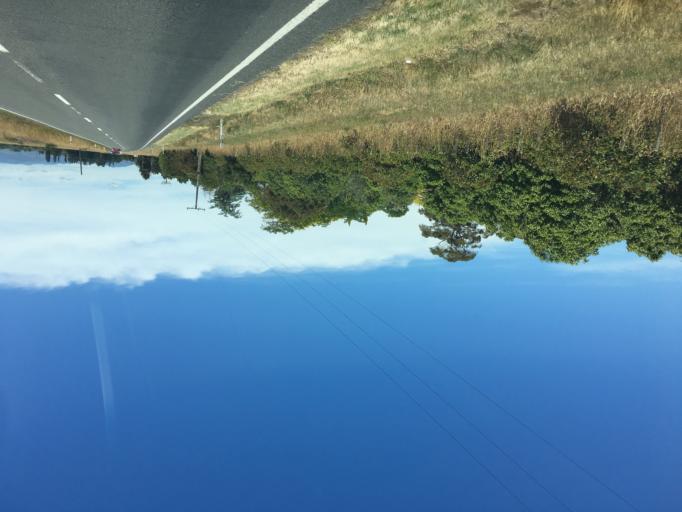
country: NZ
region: Hawke's Bay
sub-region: Hastings District
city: Hastings
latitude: -39.9976
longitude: 176.4140
